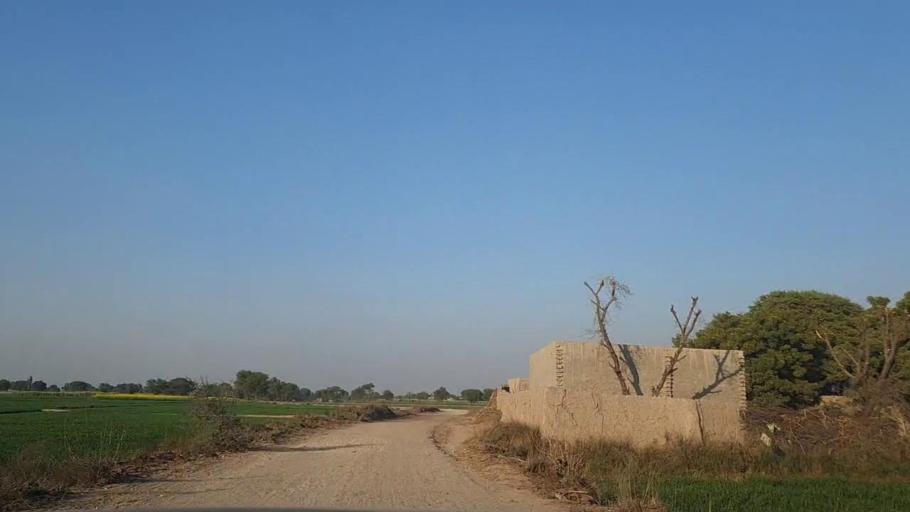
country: PK
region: Sindh
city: Sakrand
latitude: 26.3005
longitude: 68.1264
